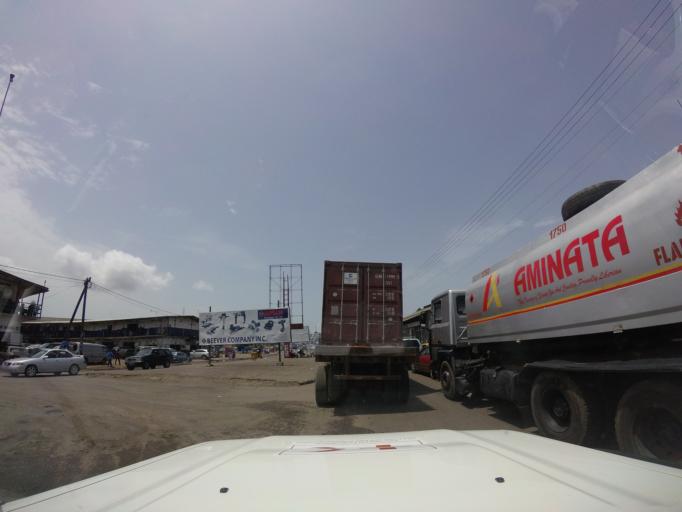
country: LR
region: Montserrado
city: Monrovia
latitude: 6.3326
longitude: -10.7984
